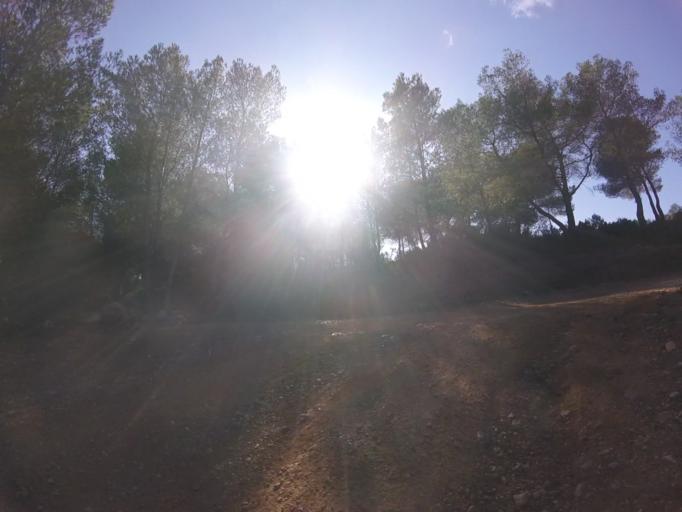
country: ES
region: Valencia
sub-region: Provincia de Castello
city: Santa Magdalena de Pulpis
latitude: 40.3050
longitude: 0.3392
